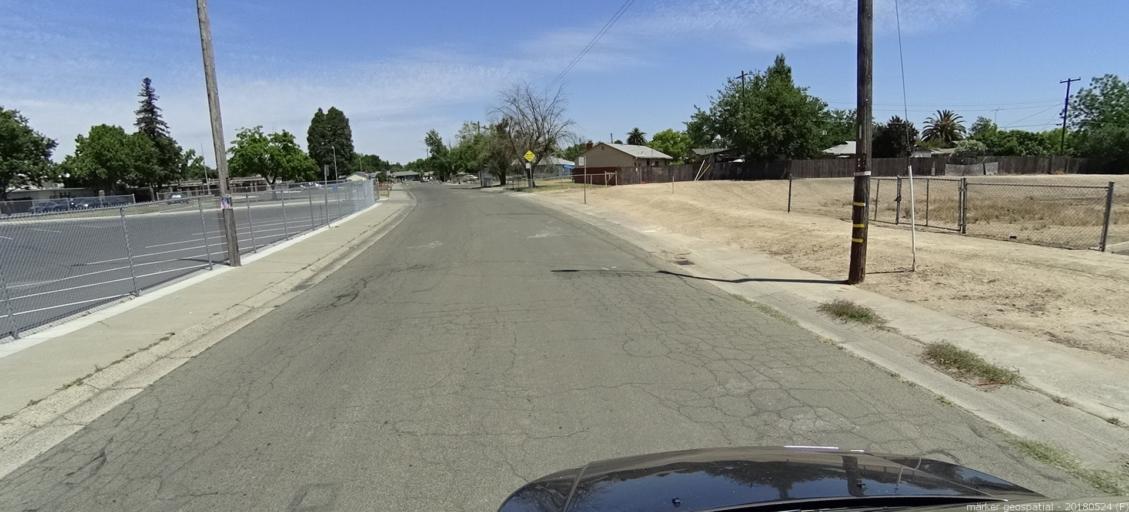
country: US
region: California
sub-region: Sacramento County
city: Sacramento
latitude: 38.6223
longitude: -121.4513
